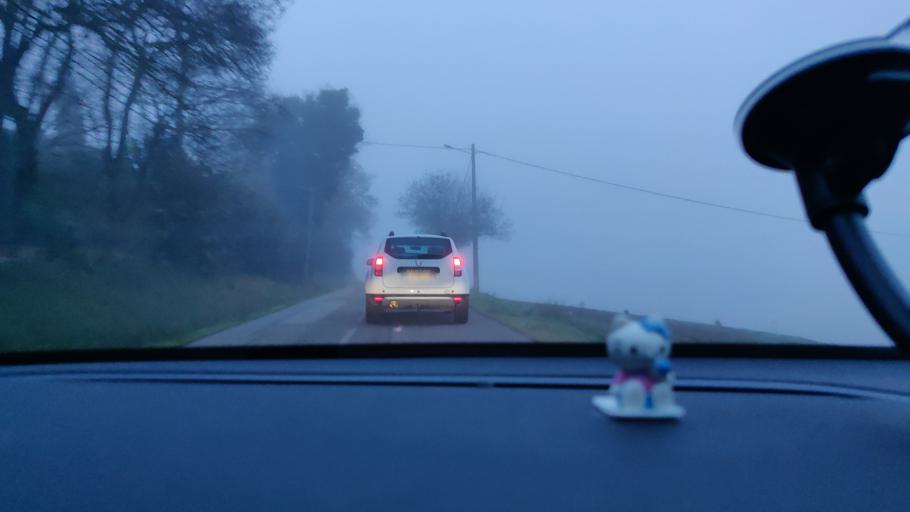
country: FR
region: Midi-Pyrenees
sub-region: Departement de la Haute-Garonne
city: Vieille-Toulouse
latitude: 43.4873
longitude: 1.4520
